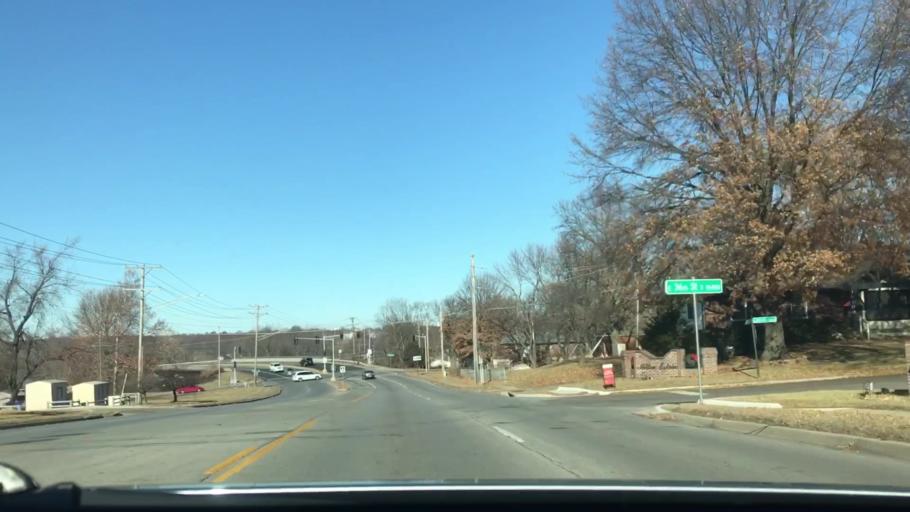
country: US
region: Missouri
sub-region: Jackson County
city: Independence
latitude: 39.0532
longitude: -94.3871
